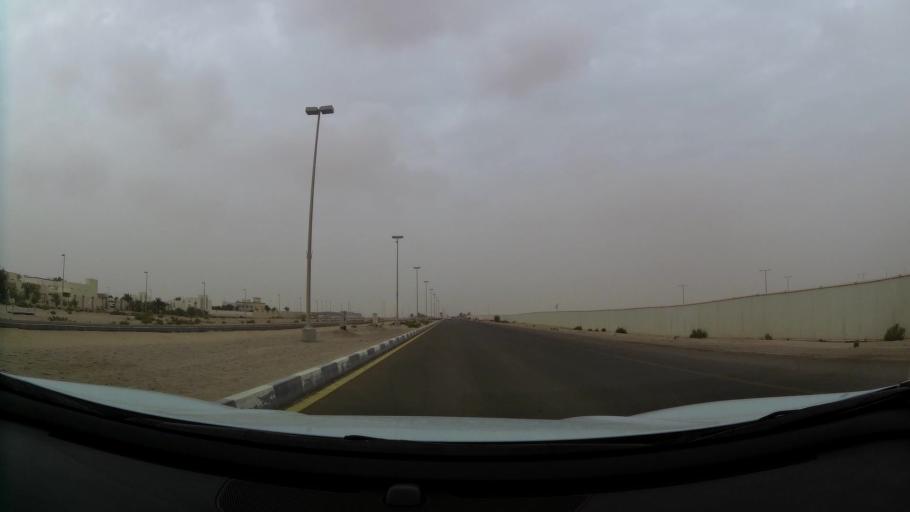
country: AE
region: Abu Dhabi
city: Abu Dhabi
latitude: 24.4264
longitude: 54.7173
